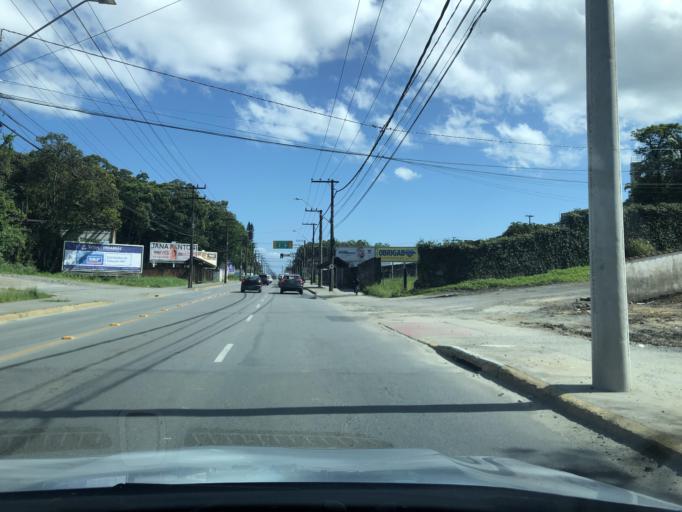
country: BR
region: Santa Catarina
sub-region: Joinville
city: Joinville
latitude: -26.2583
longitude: -48.8518
